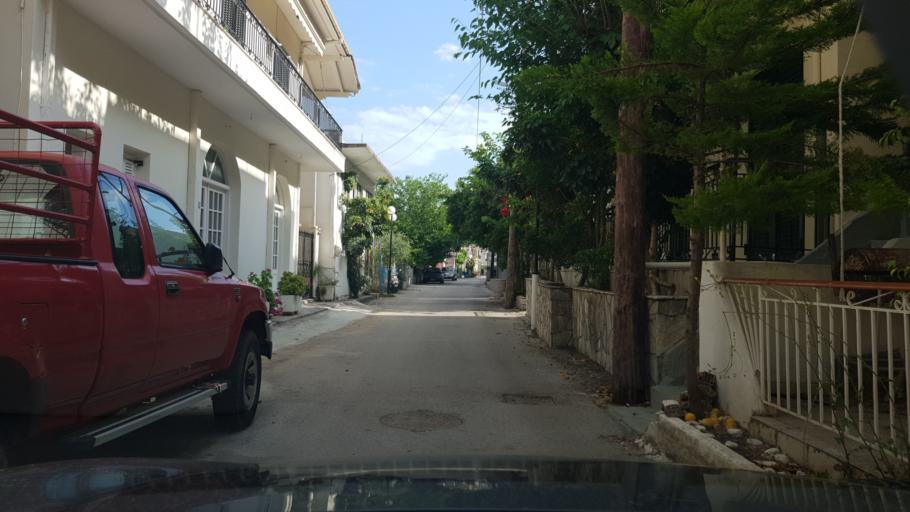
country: GR
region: Ionian Islands
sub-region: Lefkada
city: Nidri
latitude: 38.6891
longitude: 20.6984
